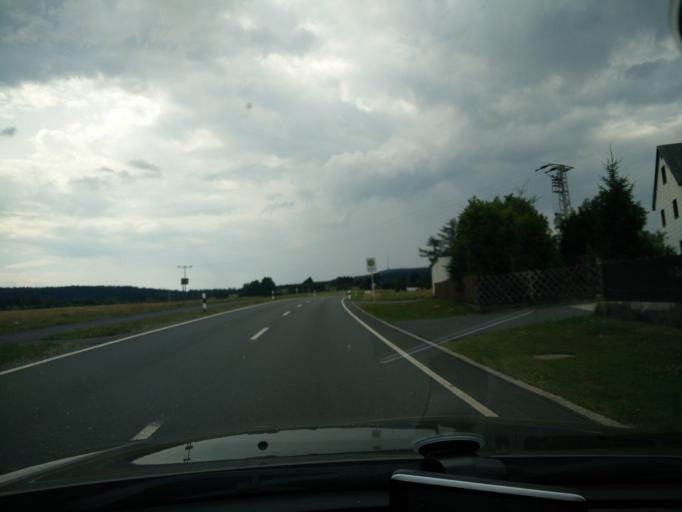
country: DE
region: Bavaria
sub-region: Upper Franconia
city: Fichtelberg
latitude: 49.9906
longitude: 11.8547
